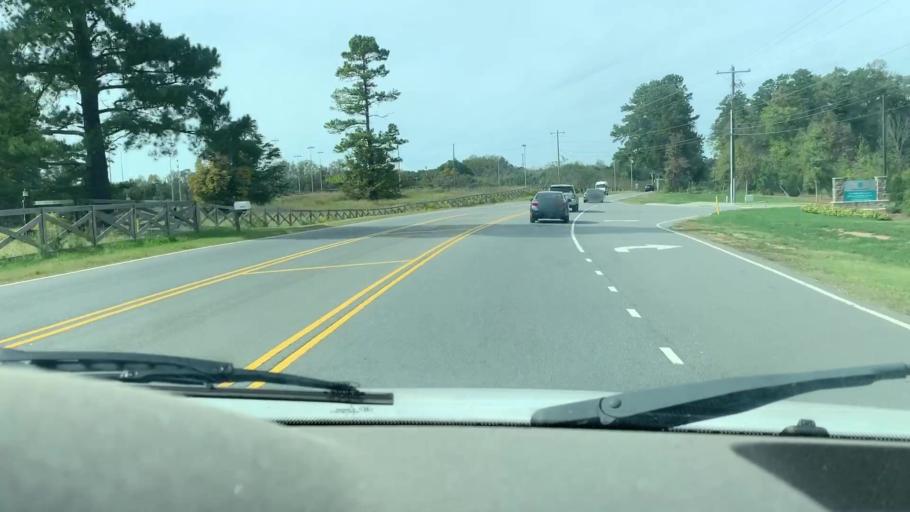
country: US
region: North Carolina
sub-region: Mecklenburg County
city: Huntersville
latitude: 35.4465
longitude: -80.7855
